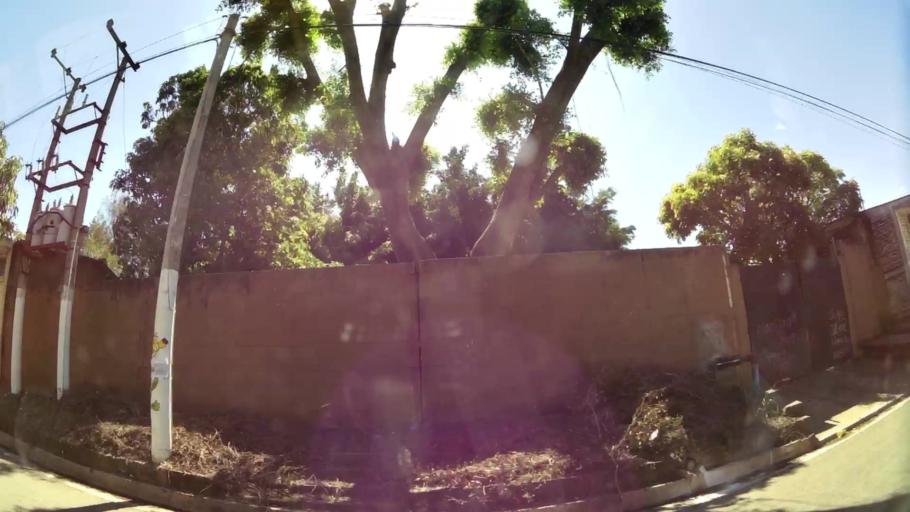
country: SV
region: Santa Ana
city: Chalchuapa
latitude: 13.9754
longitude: -89.7056
